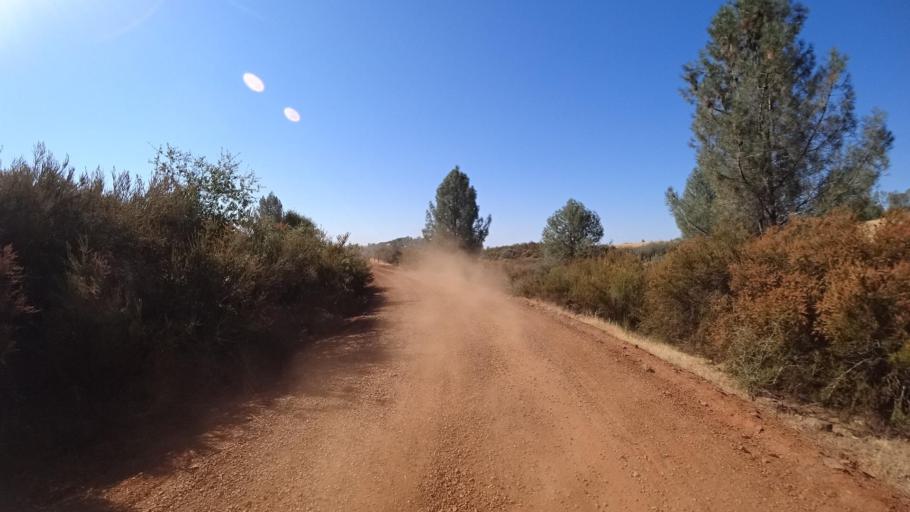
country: US
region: California
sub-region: Mariposa County
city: Mariposa
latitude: 37.6277
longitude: -120.2447
